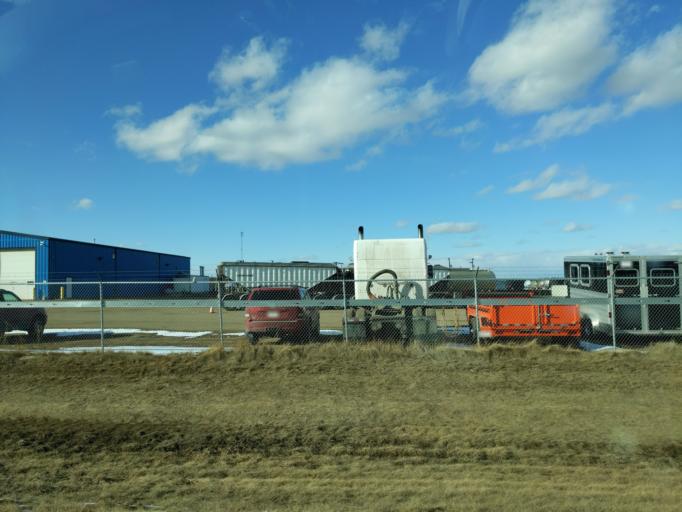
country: CA
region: Saskatchewan
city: Lloydminster
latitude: 53.2440
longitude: -109.9737
